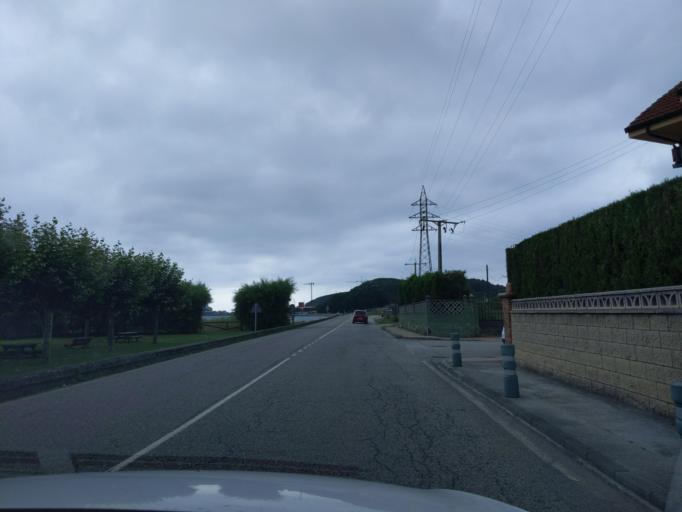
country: ES
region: Asturias
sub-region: Province of Asturias
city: Aviles
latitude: 43.5901
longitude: -5.9137
